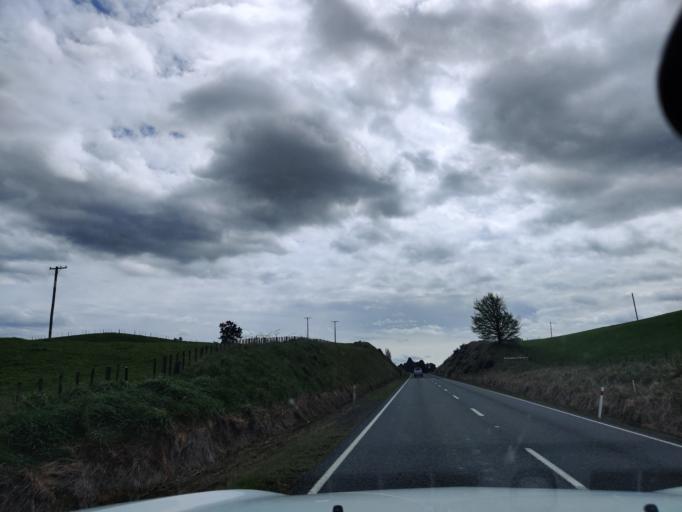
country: NZ
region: Manawatu-Wanganui
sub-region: Ruapehu District
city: Waiouru
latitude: -39.3939
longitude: 175.3733
